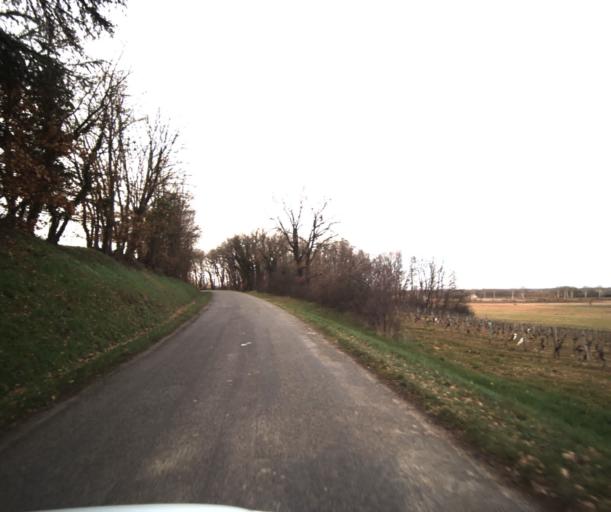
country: FR
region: Midi-Pyrenees
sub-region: Departement du Tarn-et-Garonne
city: Campsas
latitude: 43.8975
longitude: 1.3299
